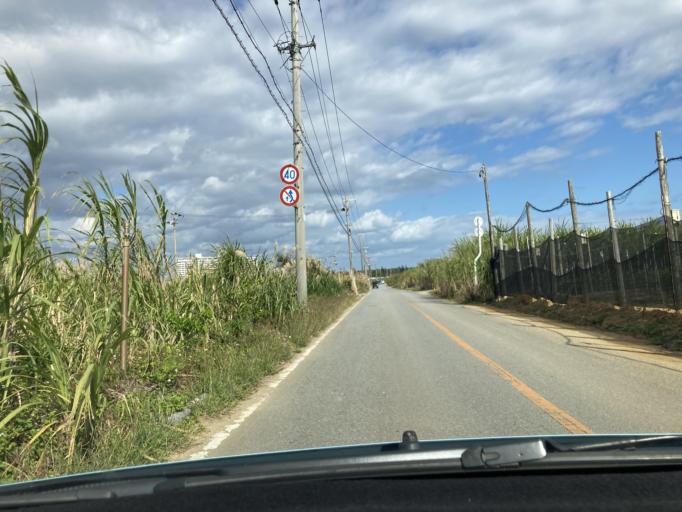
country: JP
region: Okinawa
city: Ishikawa
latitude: 26.4270
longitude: 127.7177
